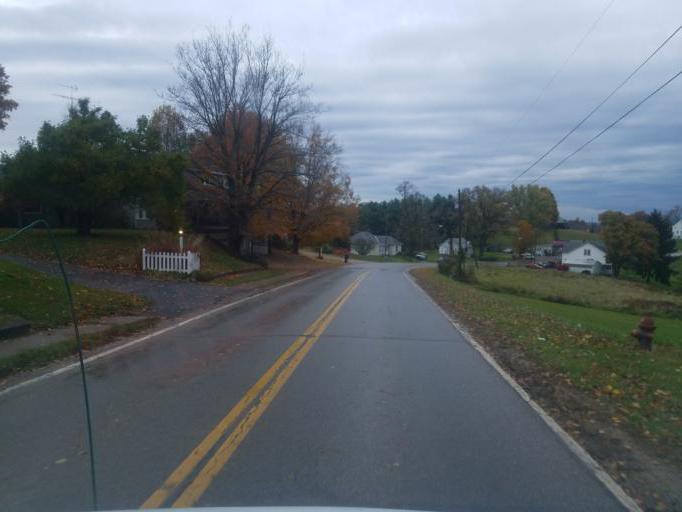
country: US
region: Ohio
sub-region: Morgan County
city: McConnelsville
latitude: 39.4947
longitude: -81.8657
